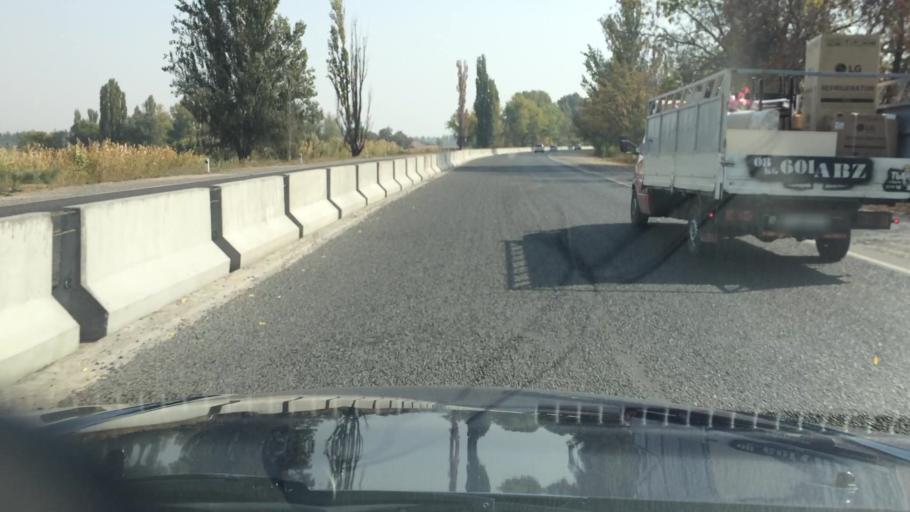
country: KG
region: Chuy
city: Kant
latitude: 42.9758
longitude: 74.8907
